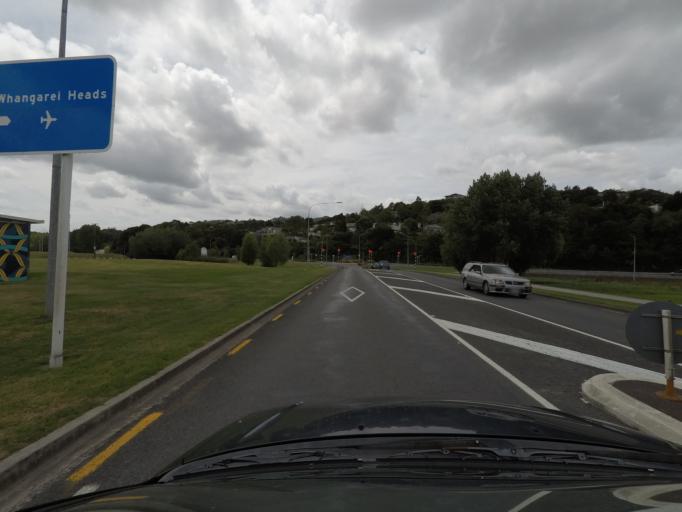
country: NZ
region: Northland
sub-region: Whangarei
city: Whangarei
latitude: -35.7322
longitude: 174.3428
